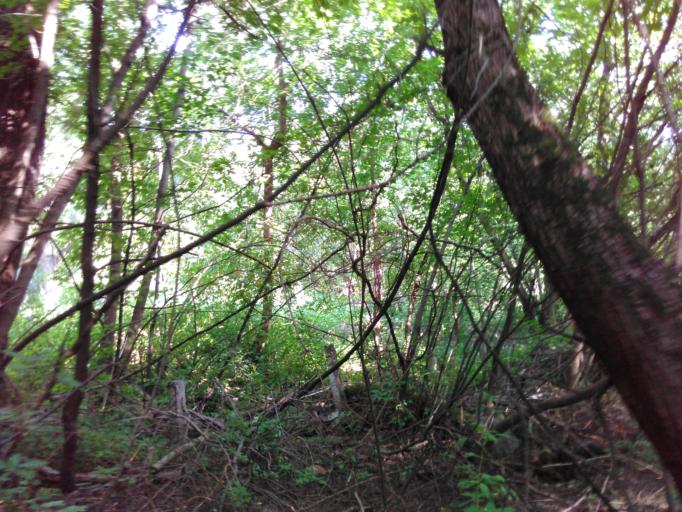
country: RU
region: Moskovskaya
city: Bol'shaya Setun'
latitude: 55.7152
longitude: 37.4283
